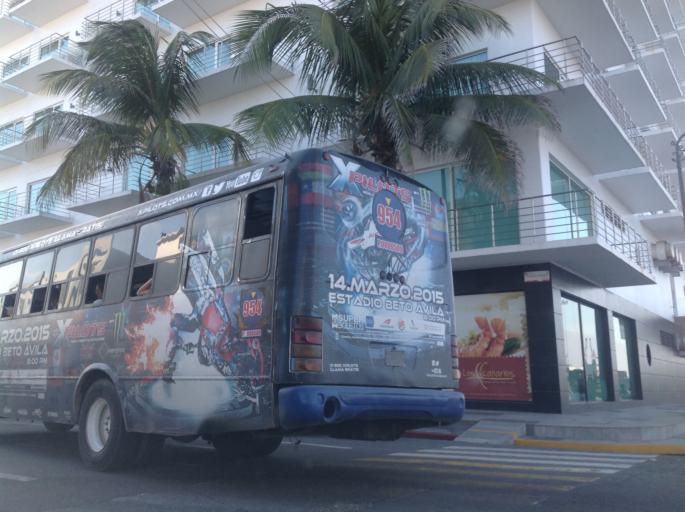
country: MX
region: Veracruz
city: Veracruz
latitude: 19.2016
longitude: -96.1338
